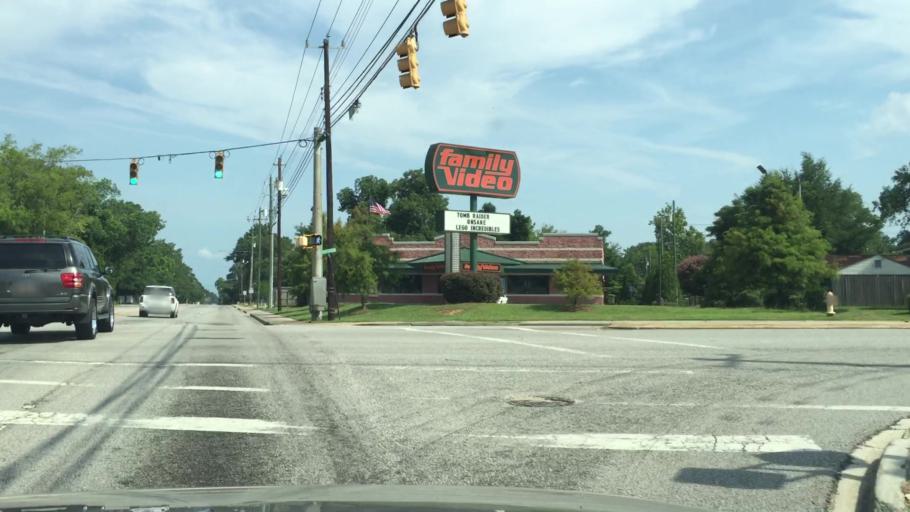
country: US
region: South Carolina
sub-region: Sumter County
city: Sumter
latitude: 33.9198
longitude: -80.3596
